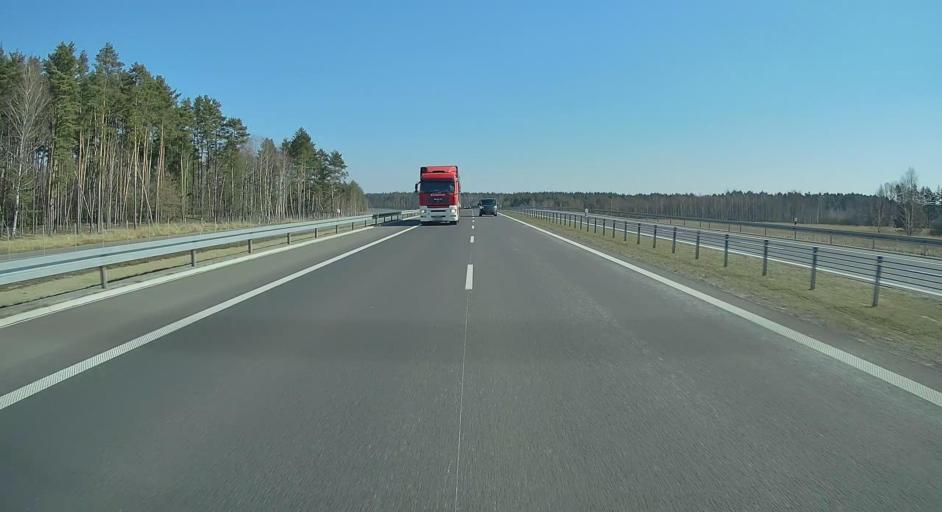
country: PL
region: Subcarpathian Voivodeship
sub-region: Powiat nizanski
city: Raclawice
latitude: 50.4745
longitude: 22.1698
